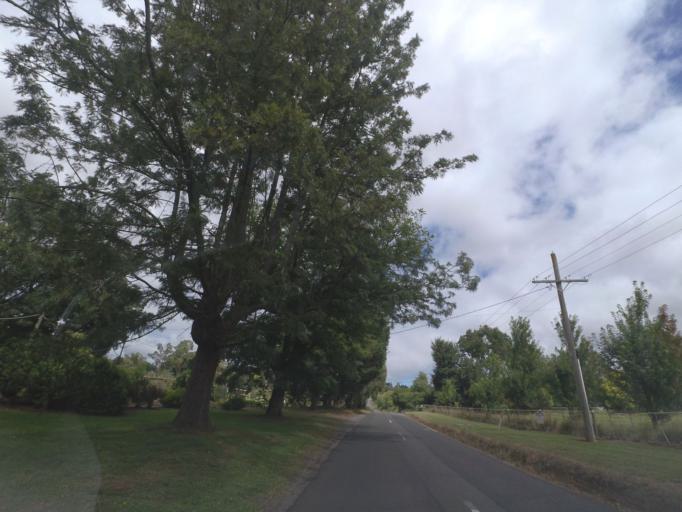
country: AU
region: Victoria
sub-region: Yarra Ranges
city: Mount Evelyn
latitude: -37.7932
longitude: 145.4483
